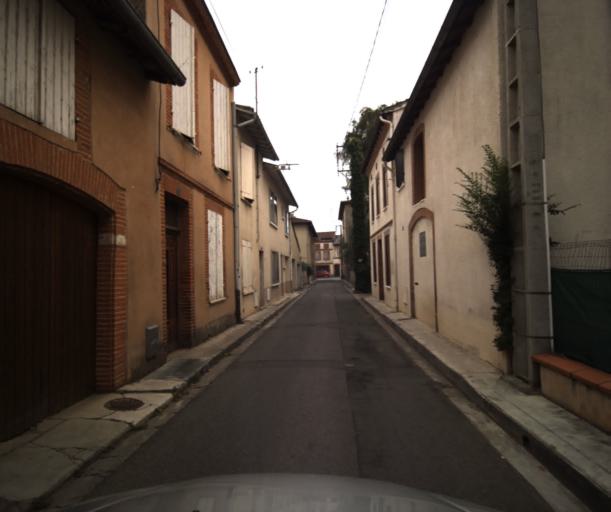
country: FR
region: Midi-Pyrenees
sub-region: Departement de la Haute-Garonne
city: Muret
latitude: 43.4586
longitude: 1.3246
